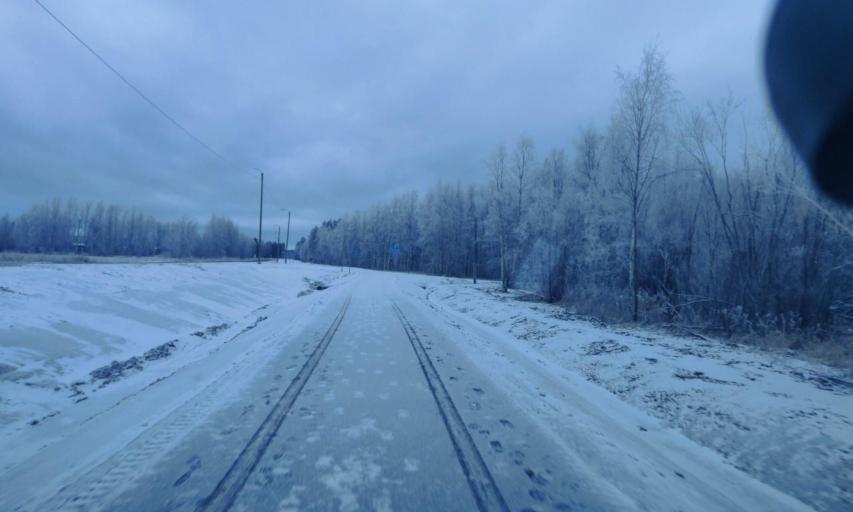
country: FI
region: Northern Ostrobothnia
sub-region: Oulu
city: Oulunsalo
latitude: 64.9824
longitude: 25.2709
